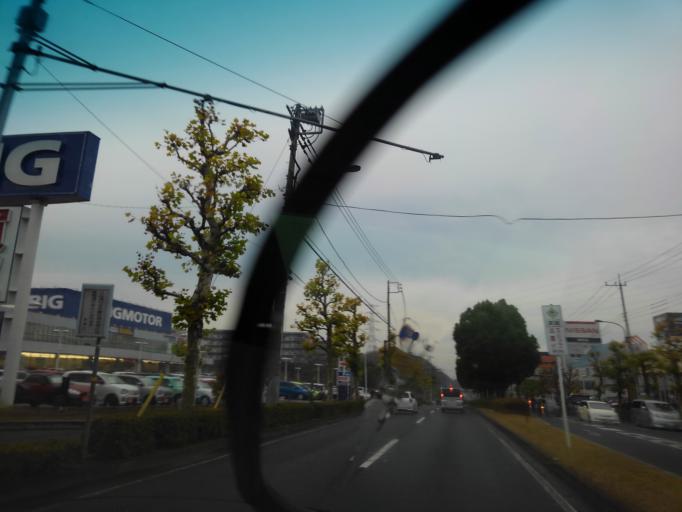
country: JP
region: Tokyo
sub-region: Machida-shi
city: Machida
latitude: 35.6117
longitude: 139.4429
